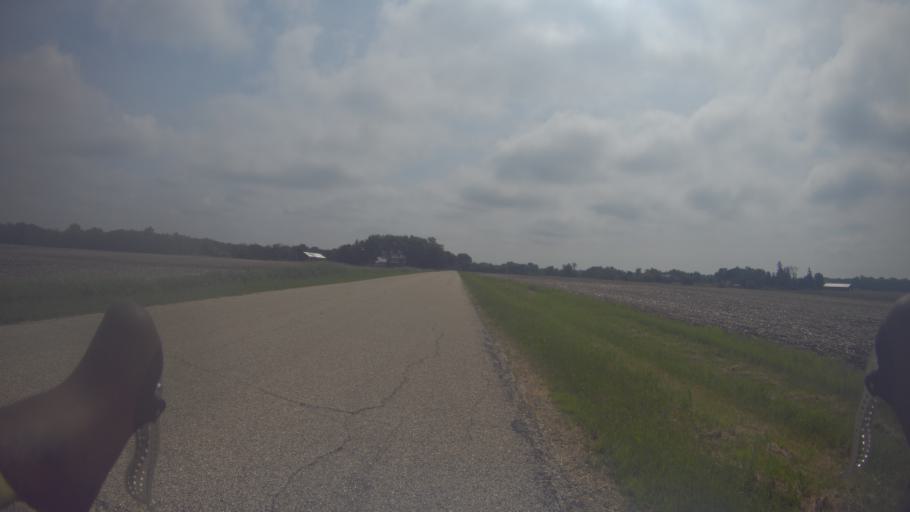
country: US
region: Wisconsin
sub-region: Jefferson County
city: Cambridge
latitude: 42.9204
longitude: -89.0376
